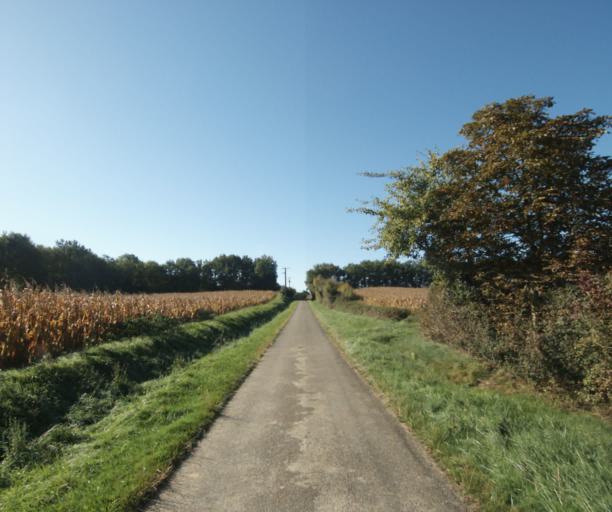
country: FR
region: Midi-Pyrenees
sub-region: Departement du Gers
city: Gondrin
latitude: 43.8136
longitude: 0.2324
